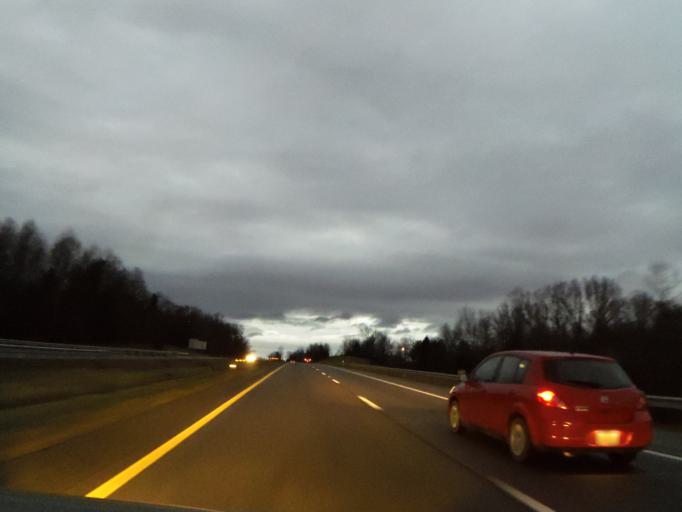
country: US
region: Tennessee
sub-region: Washington County
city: Gray
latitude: 36.4148
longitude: -82.4888
